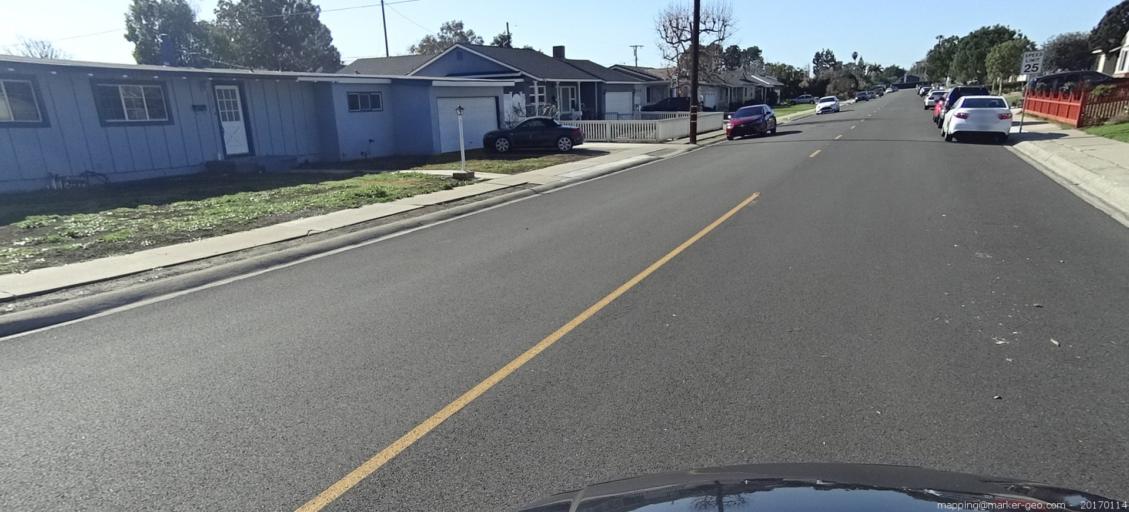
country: US
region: California
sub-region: Orange County
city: Tustin
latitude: 33.7544
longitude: -117.8181
